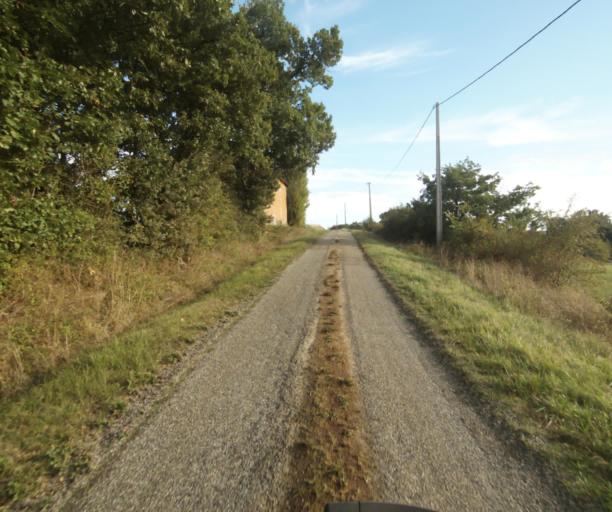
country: FR
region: Midi-Pyrenees
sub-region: Departement du Tarn-et-Garonne
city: Finhan
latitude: 43.9158
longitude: 1.1088
